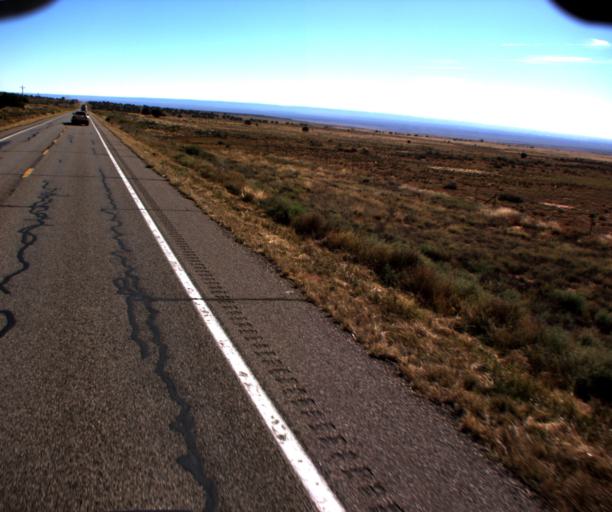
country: US
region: Arizona
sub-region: Mohave County
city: Colorado City
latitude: 36.8582
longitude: -112.7906
